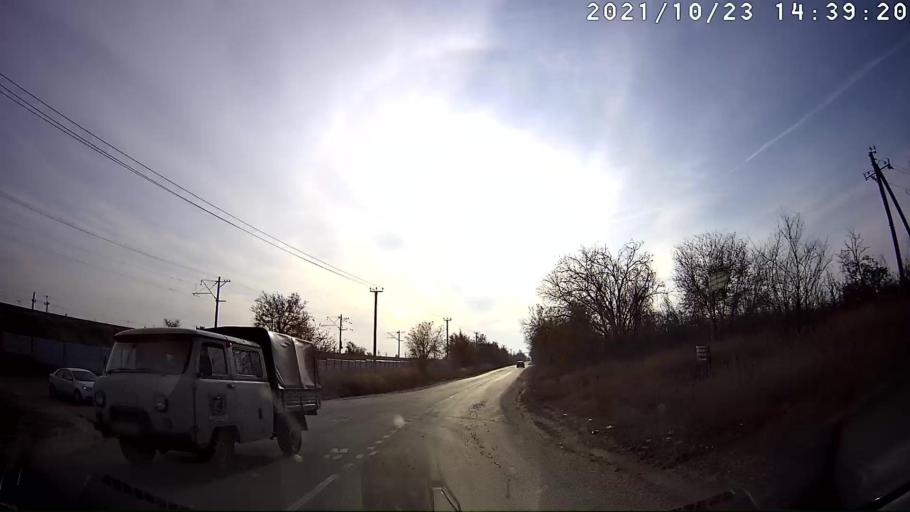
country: RU
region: Volgograd
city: Krasnoslobodsk
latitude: 48.4858
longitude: 44.5457
